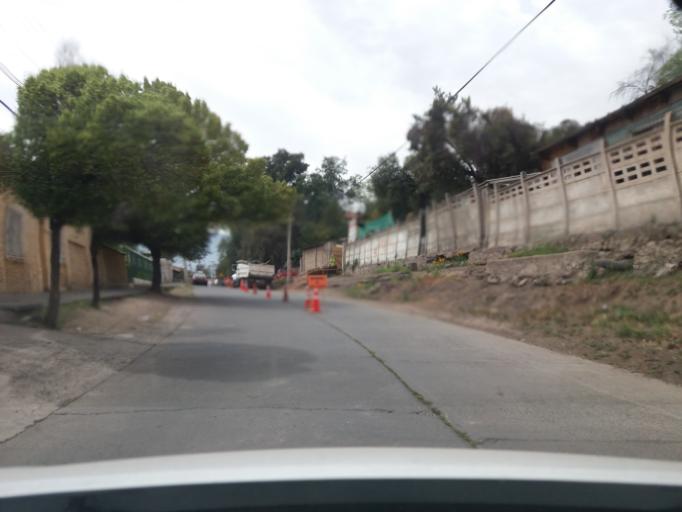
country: CL
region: Valparaiso
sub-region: Provincia de Los Andes
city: Los Andes
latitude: -32.8351
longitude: -70.5914
